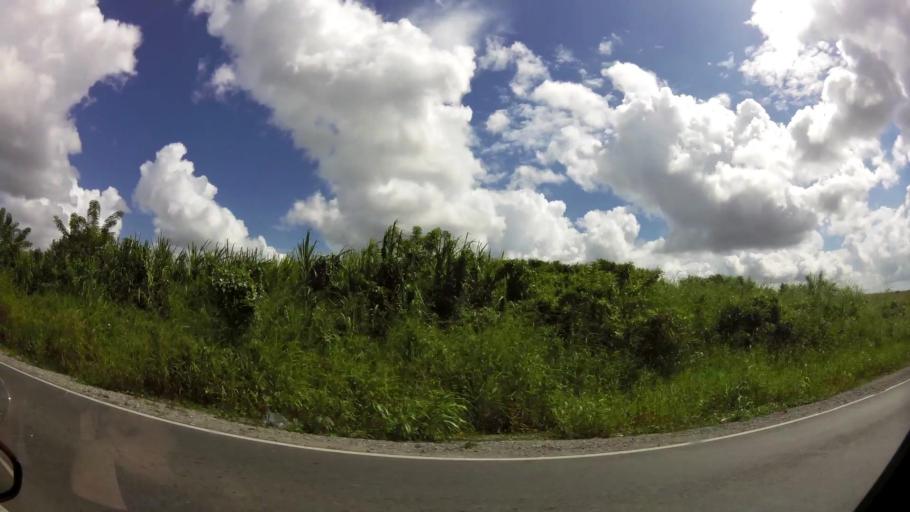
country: TT
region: Penal/Debe
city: Debe
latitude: 10.2198
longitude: -61.4643
